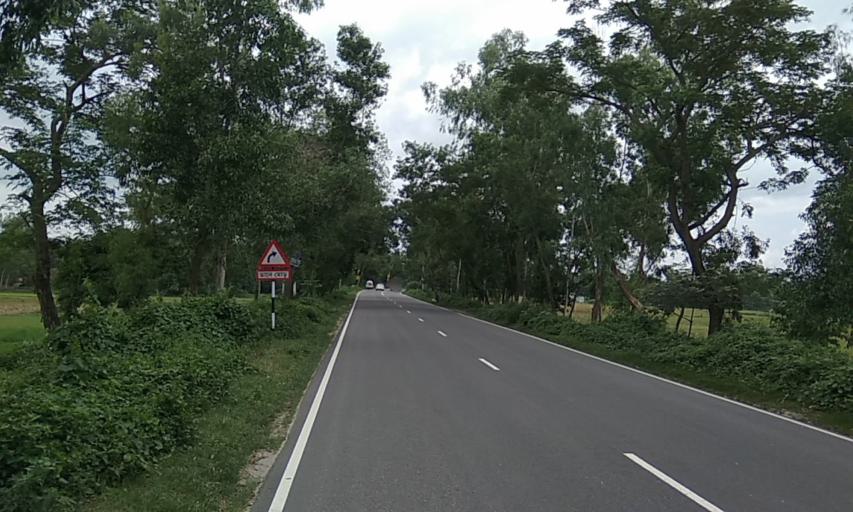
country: BD
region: Rangpur Division
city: Rangpur
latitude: 25.8016
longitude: 89.1860
